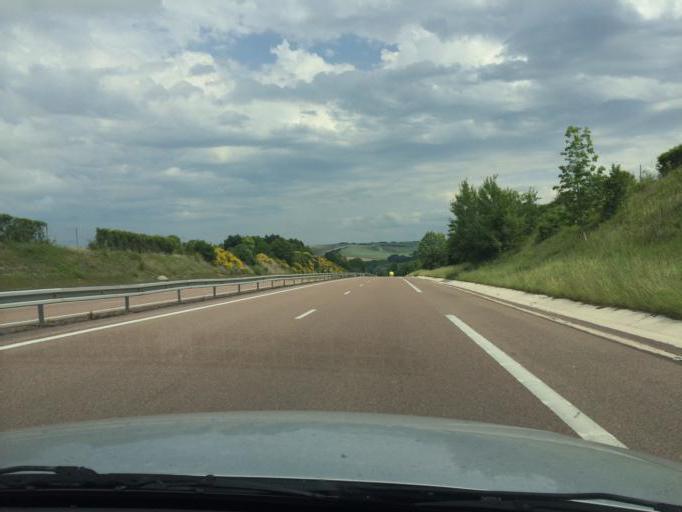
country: FR
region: Champagne-Ardenne
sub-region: Departement de la Marne
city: Jonchery-sur-Vesle
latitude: 49.2148
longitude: 3.7998
